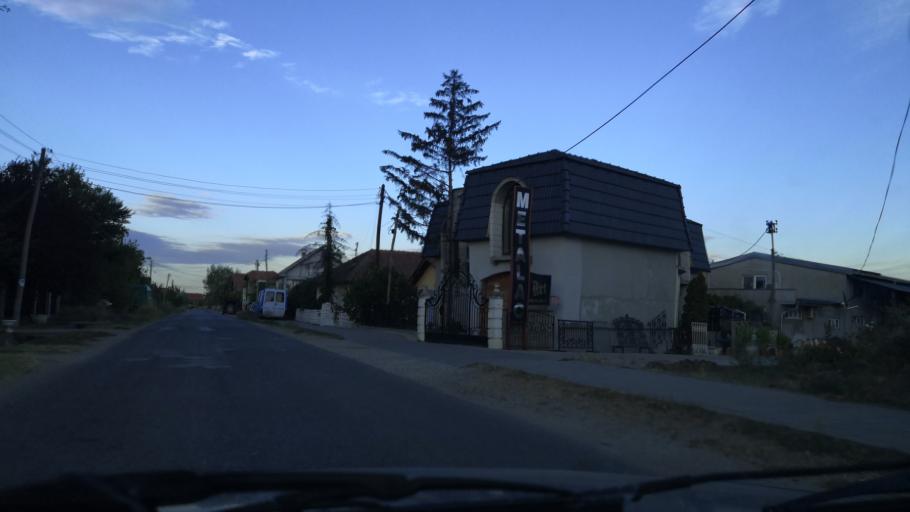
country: RS
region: Central Serbia
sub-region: Borski Okrug
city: Negotin
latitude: 44.2345
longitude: 22.5433
